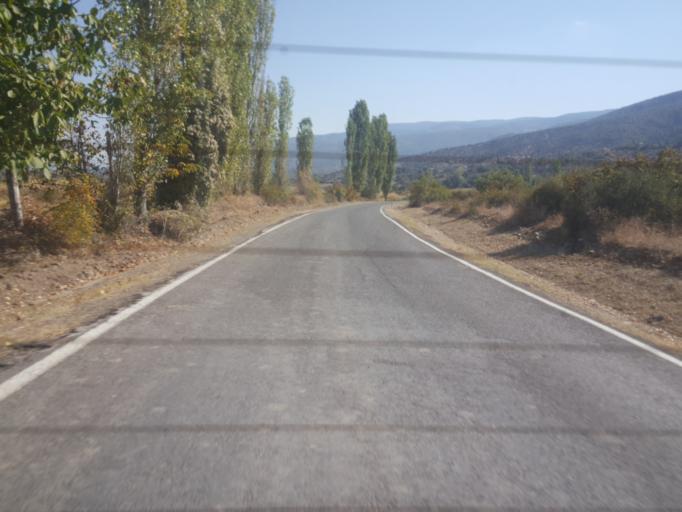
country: TR
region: Kastamonu
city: Tosya
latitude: 40.9928
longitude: 34.1180
